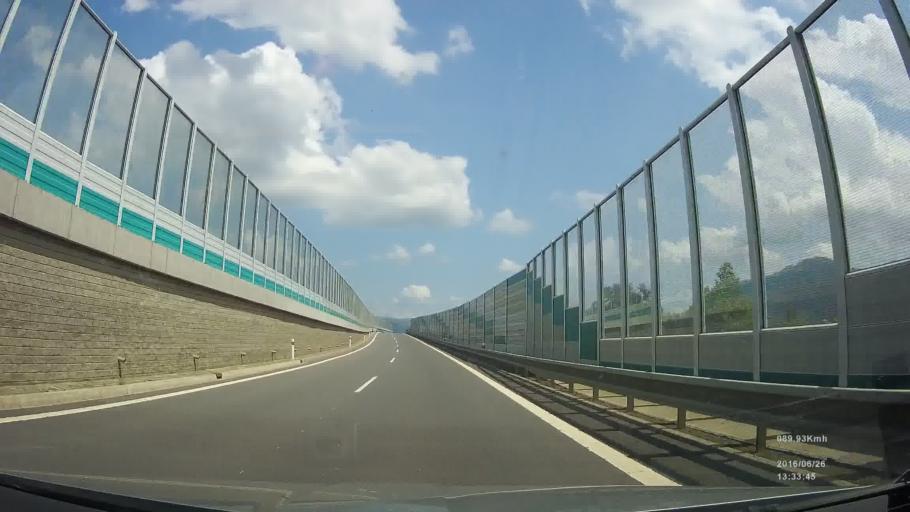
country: SK
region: Banskobystricky
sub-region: Okres Banska Bystrica
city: Banska Bystrica
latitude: 48.7431
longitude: 19.1600
